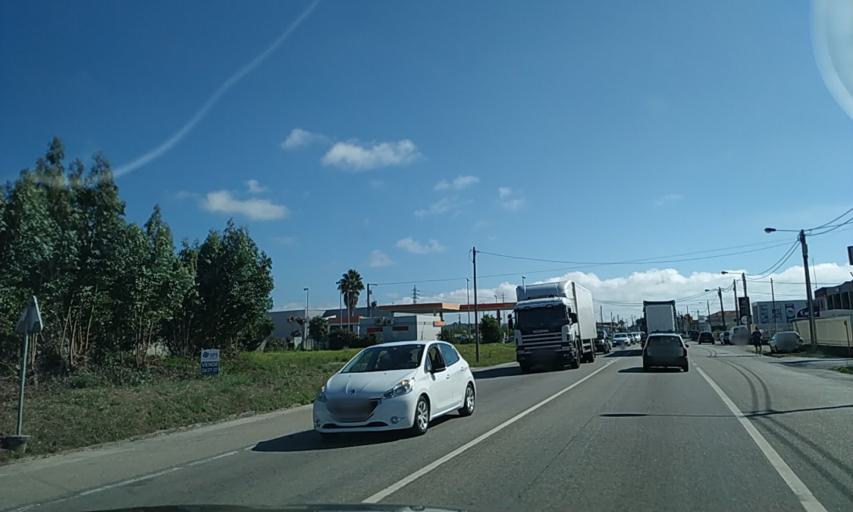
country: PT
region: Aveiro
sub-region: Aveiro
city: Aveiro
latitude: 40.6668
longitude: -8.6092
